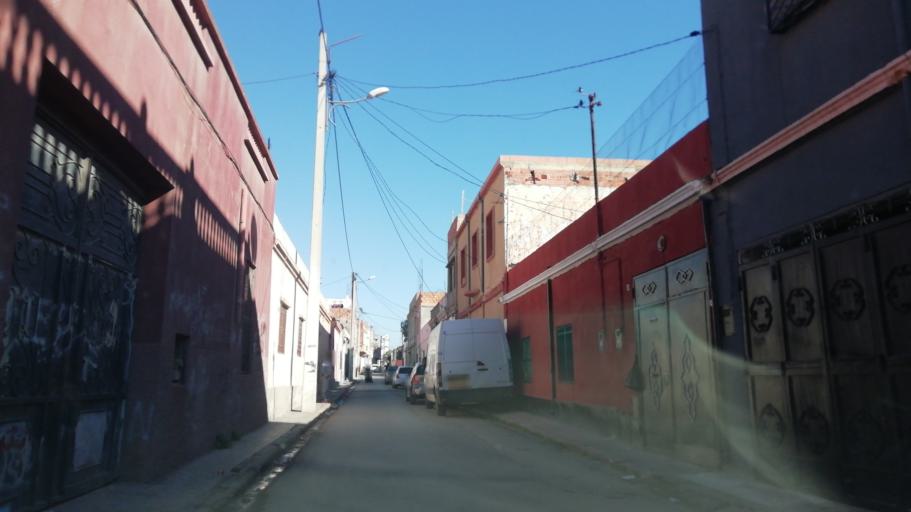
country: DZ
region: Oran
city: Oran
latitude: 35.7030
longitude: -0.6140
